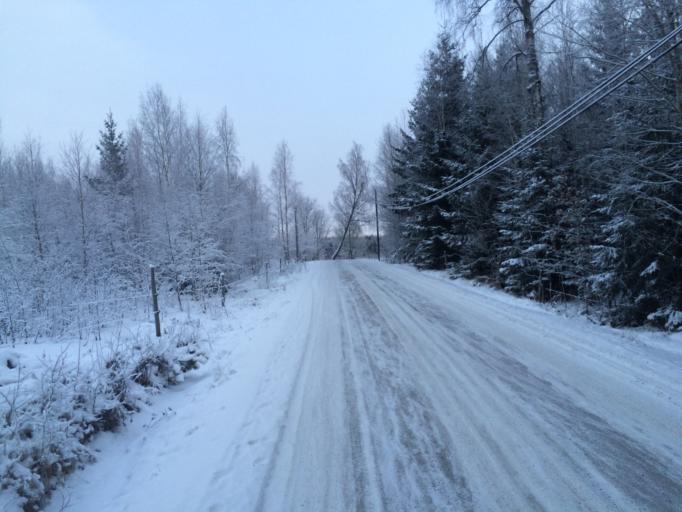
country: SE
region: Uppsala
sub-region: Enkopings Kommun
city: Orsundsbro
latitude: 59.9090
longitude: 17.1829
